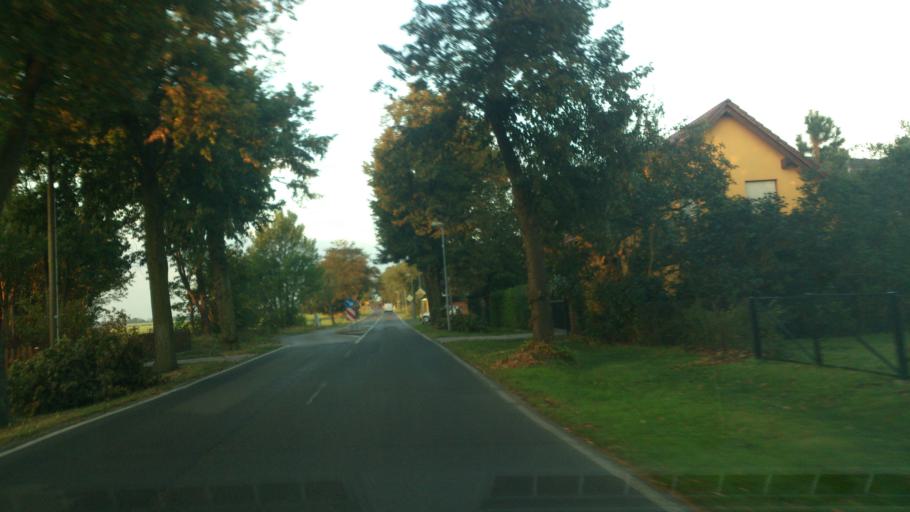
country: DE
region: Brandenburg
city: Rangsdorf
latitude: 52.2701
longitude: 13.3532
